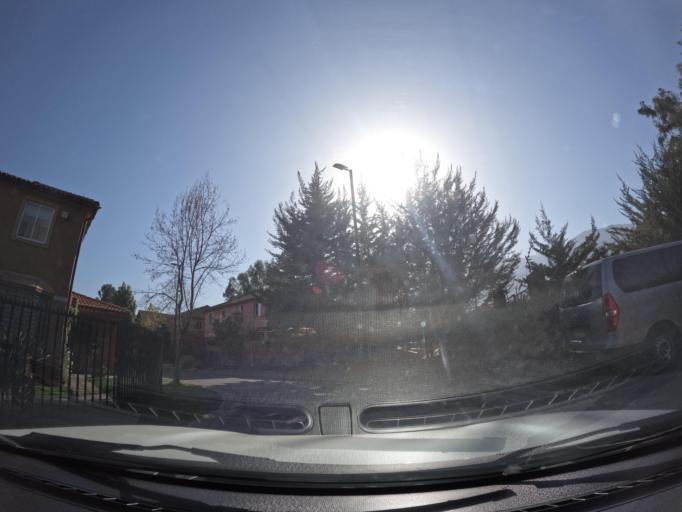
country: CL
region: Santiago Metropolitan
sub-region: Provincia de Santiago
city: Villa Presidente Frei, Nunoa, Santiago, Chile
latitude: -33.5116
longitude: -70.5463
